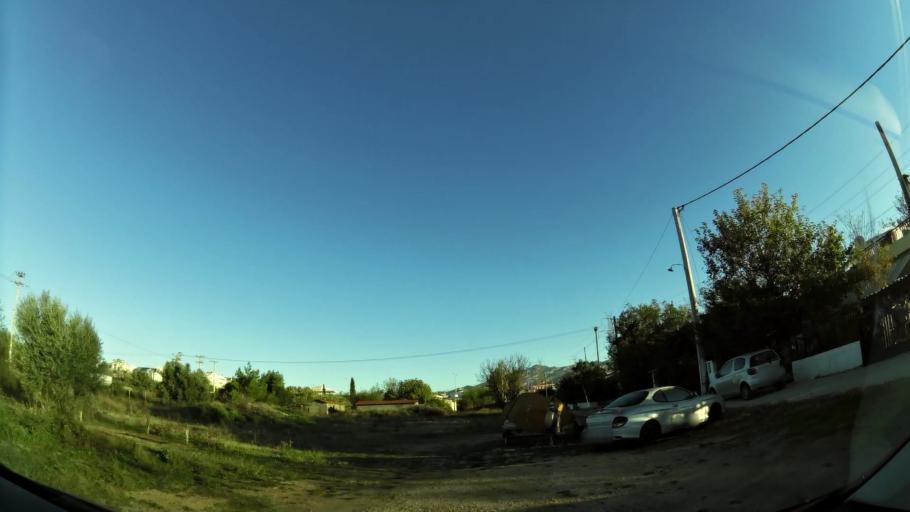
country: GR
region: Attica
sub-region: Nomarchia Anatolikis Attikis
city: Pallini
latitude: 38.0055
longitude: 23.8625
